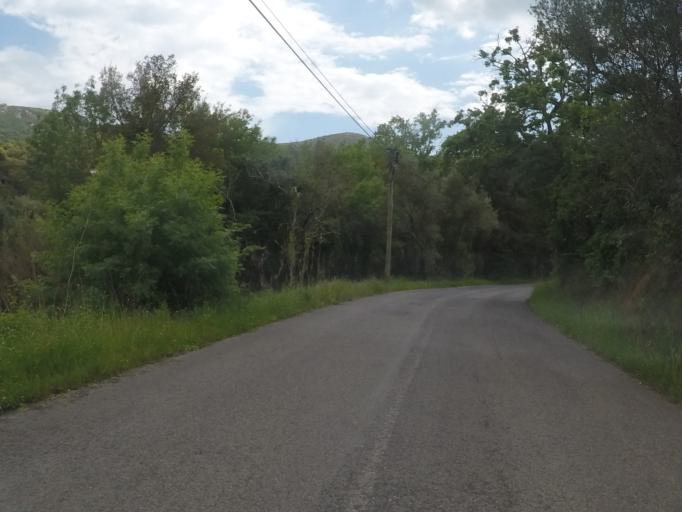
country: PT
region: Setubal
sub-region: Palmela
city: Quinta do Anjo
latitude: 38.5043
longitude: -8.9828
